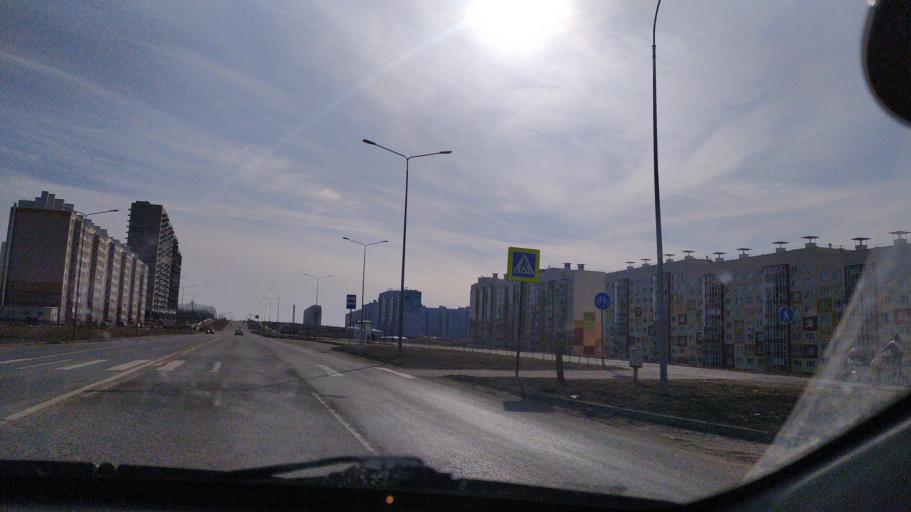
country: RU
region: Chuvashia
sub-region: Cheboksarskiy Rayon
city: Cheboksary
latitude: 56.1203
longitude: 47.2164
